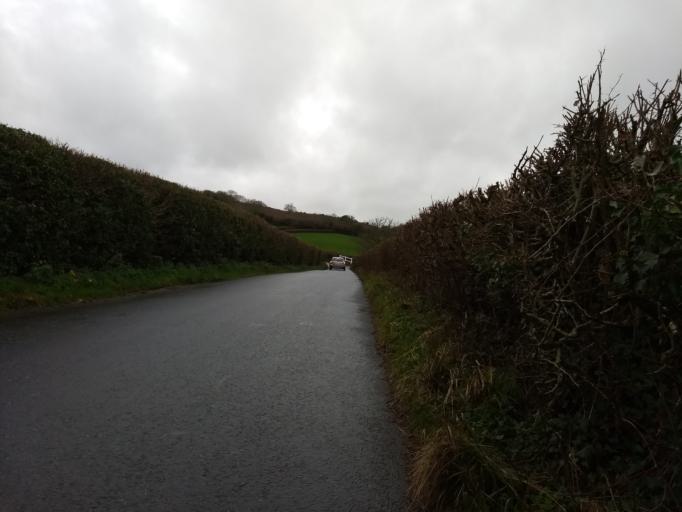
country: GB
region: England
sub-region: Isle of Wight
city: Newport
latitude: 50.6889
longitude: -1.2741
